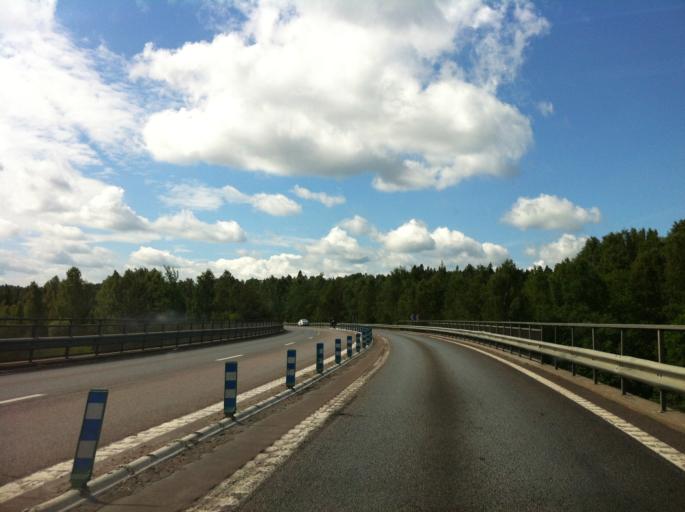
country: SE
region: Vaermland
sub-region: Grums Kommun
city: Grums
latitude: 59.3463
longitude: 13.1156
